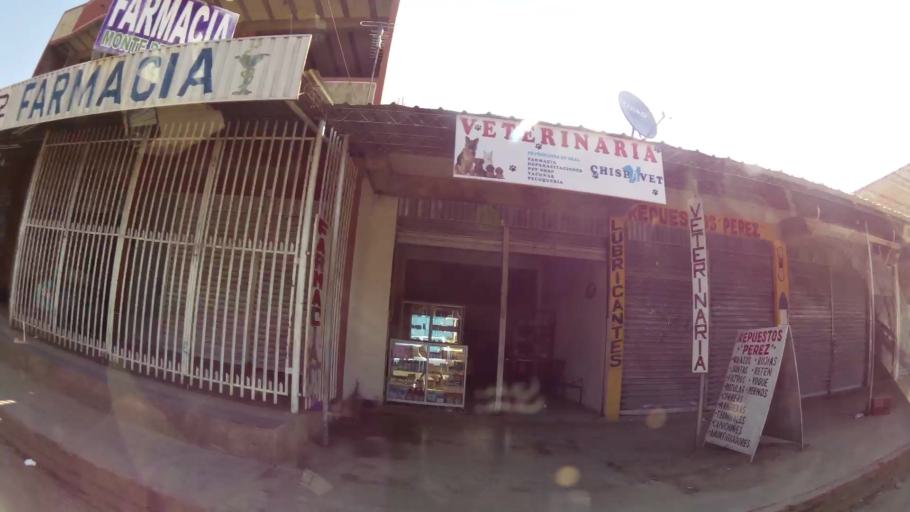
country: BO
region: Santa Cruz
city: Cotoca
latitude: -17.7396
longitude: -63.0741
